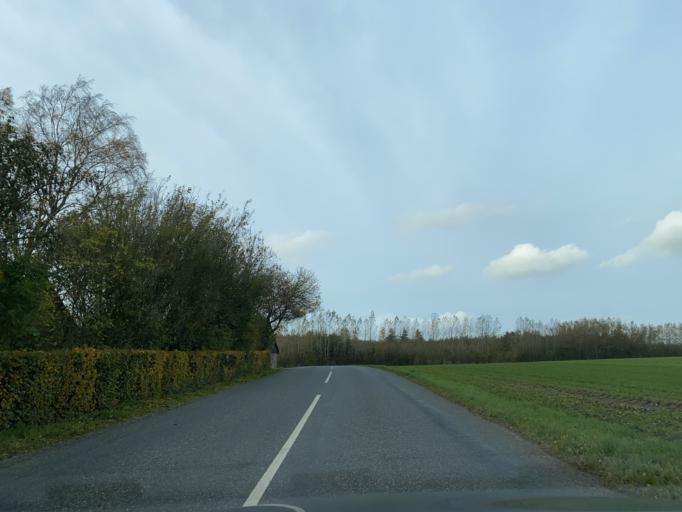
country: DK
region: Central Jutland
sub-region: Skanderborg Kommune
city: Ry
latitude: 56.1916
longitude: 9.7641
